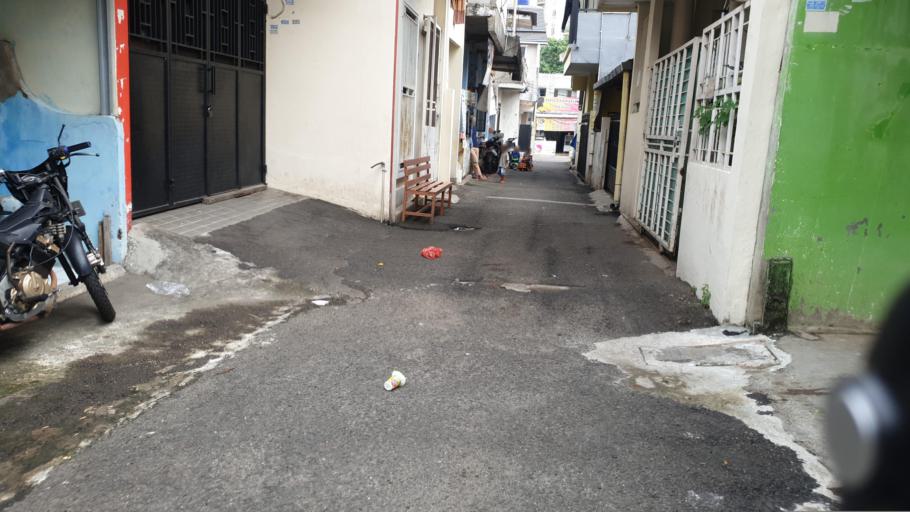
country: ID
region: West Java
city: Ciputat
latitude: -6.1958
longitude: 106.7581
